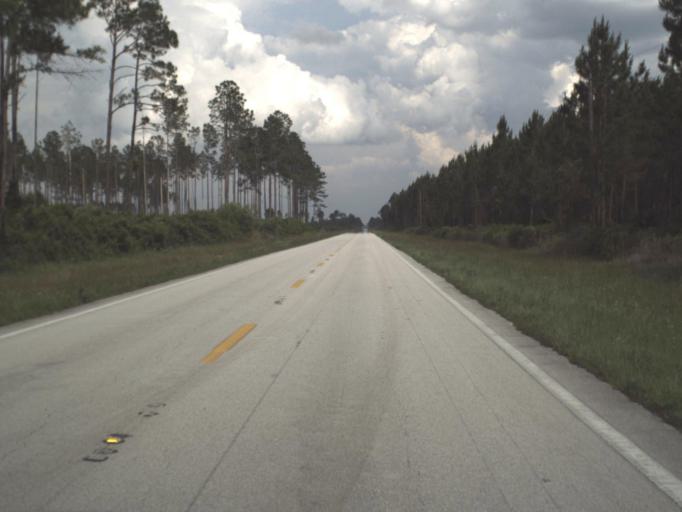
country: US
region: Florida
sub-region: Baker County
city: Macclenny
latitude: 30.5423
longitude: -82.3398
